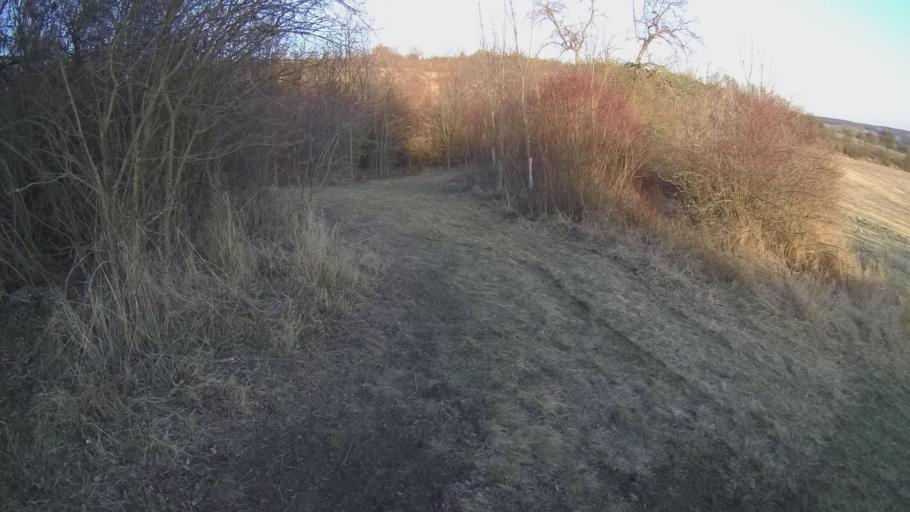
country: CZ
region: Ustecky
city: Roudnice nad Labem
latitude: 50.3781
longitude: 14.2853
